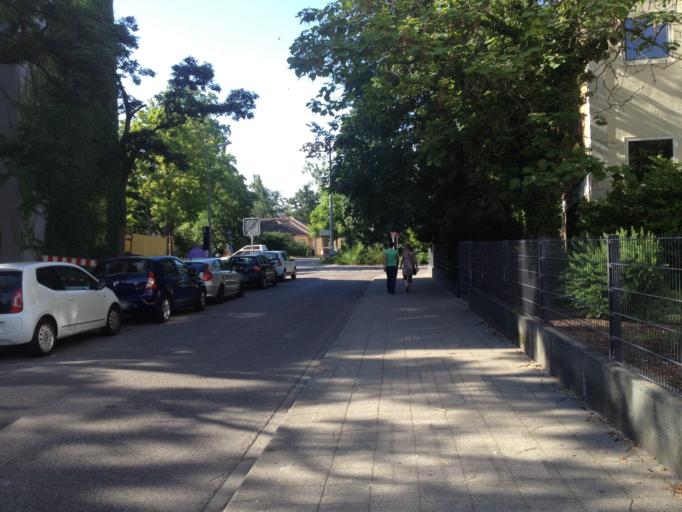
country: DE
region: Baden-Wuerttemberg
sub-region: Karlsruhe Region
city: Karlsruhe
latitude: 49.0139
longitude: 8.3940
